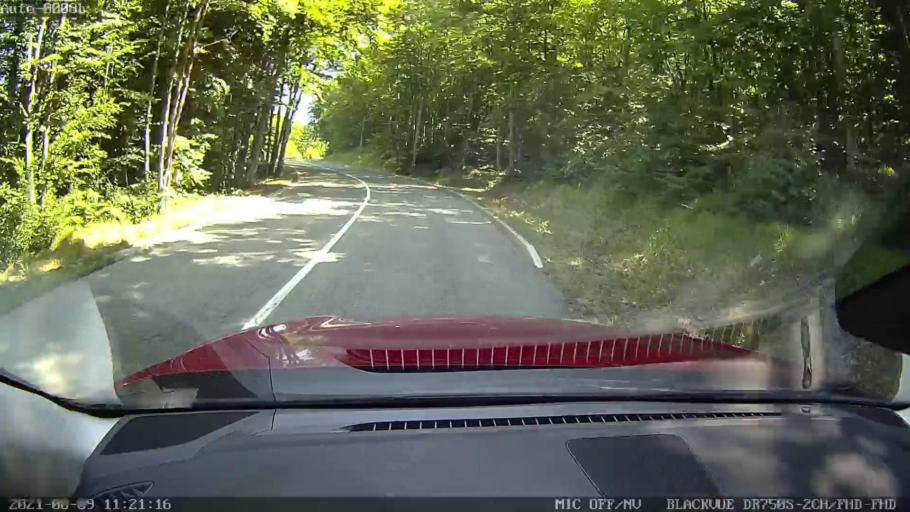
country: HR
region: Istarska
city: Lovran
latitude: 45.3034
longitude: 14.1994
